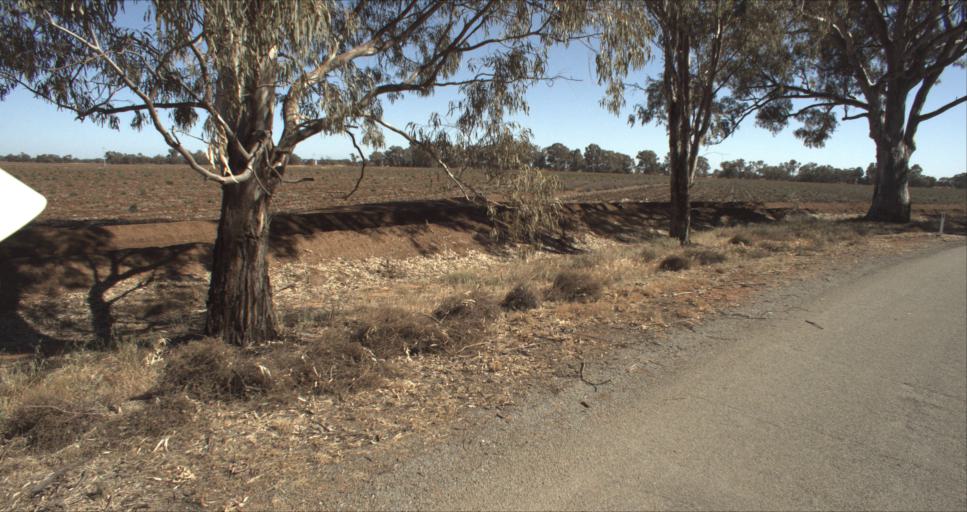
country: AU
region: New South Wales
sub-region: Leeton
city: Leeton
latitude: -34.6102
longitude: 146.2601
